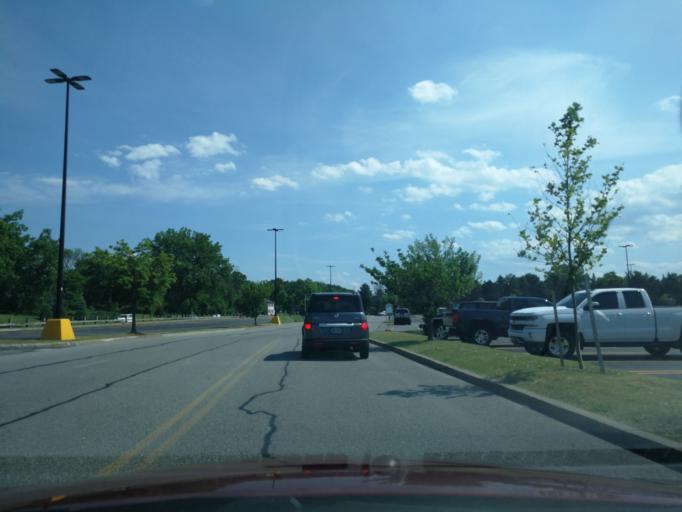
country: US
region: New York
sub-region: Monroe County
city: Greece
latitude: 43.2069
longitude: -77.6862
